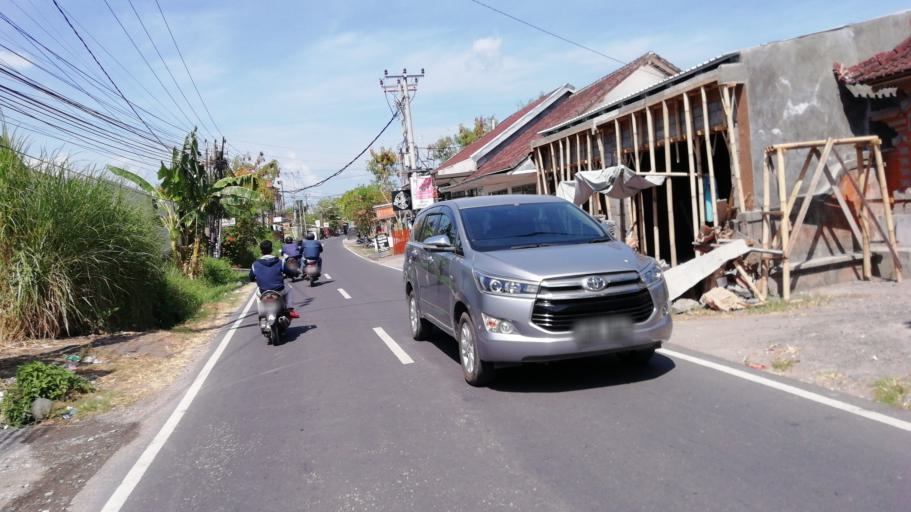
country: ID
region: Bali
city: Banjar Gunungpande
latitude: -8.6451
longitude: 115.1413
